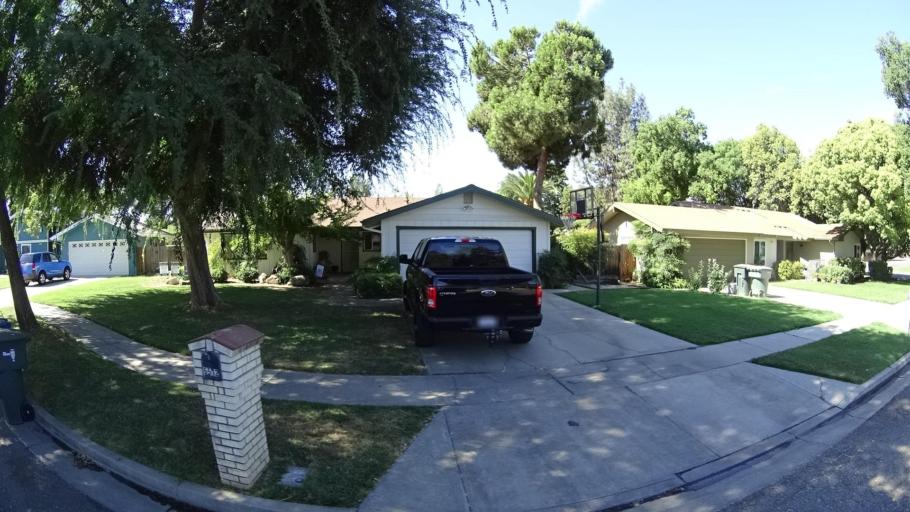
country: US
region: California
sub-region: Fresno County
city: Sunnyside
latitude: 36.7445
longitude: -119.7042
